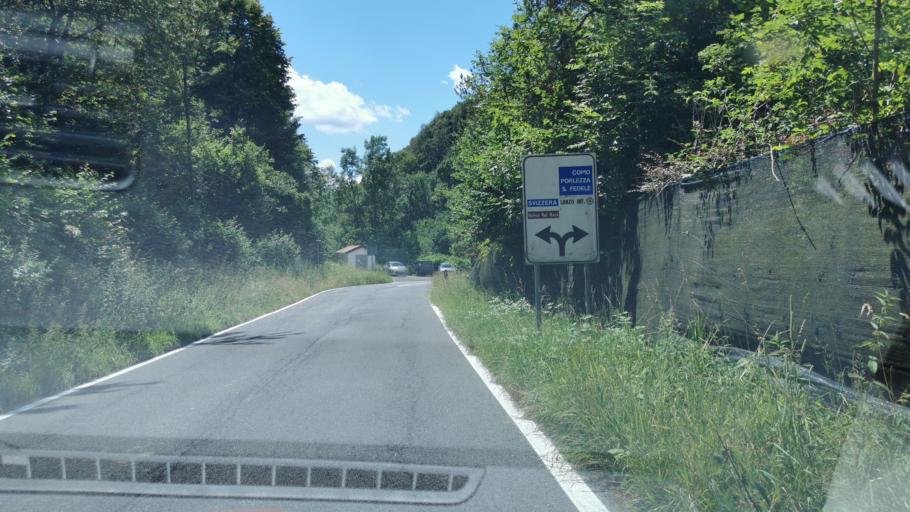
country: IT
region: Lombardy
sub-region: Provincia di Como
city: Lanzo d'Intelvi
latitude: 45.9688
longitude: 9.0238
